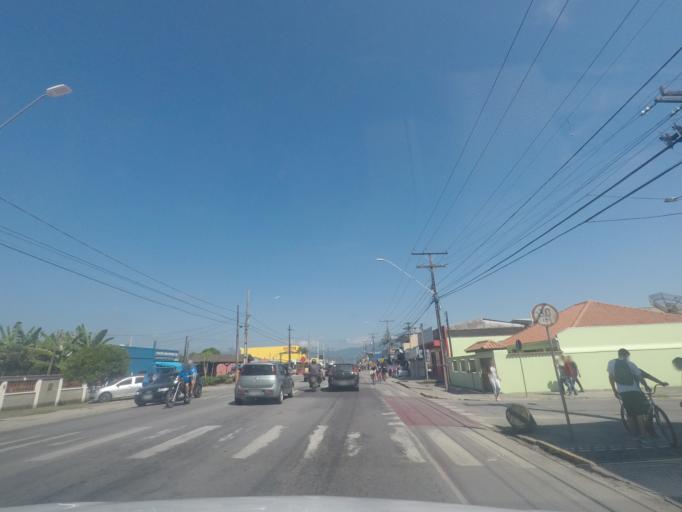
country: BR
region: Parana
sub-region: Paranagua
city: Paranagua
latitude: -25.5582
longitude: -48.5585
